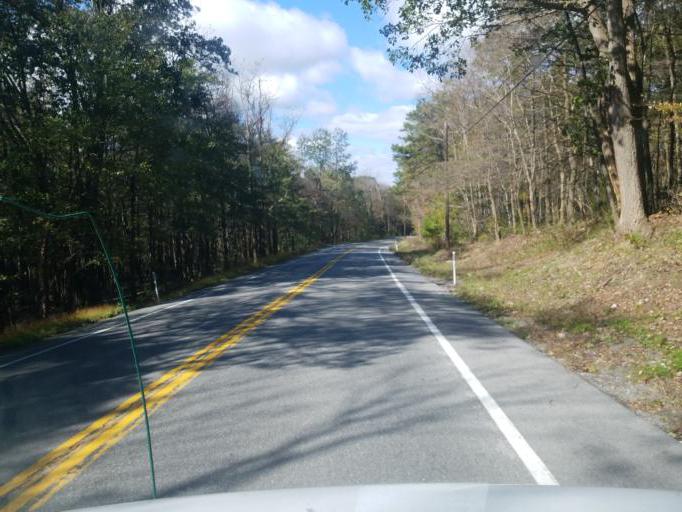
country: US
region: Pennsylvania
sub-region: Fulton County
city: McConnellsburg
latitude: 40.0201
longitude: -78.1660
